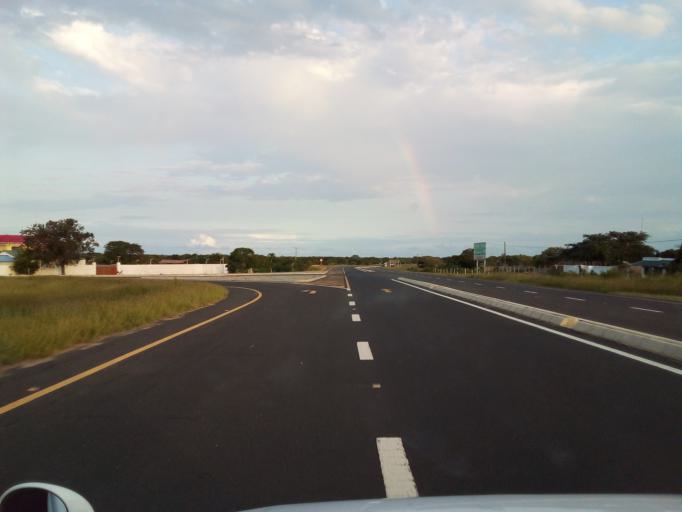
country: MZ
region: Maputo City
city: Maputo
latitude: -26.0790
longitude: 32.6193
